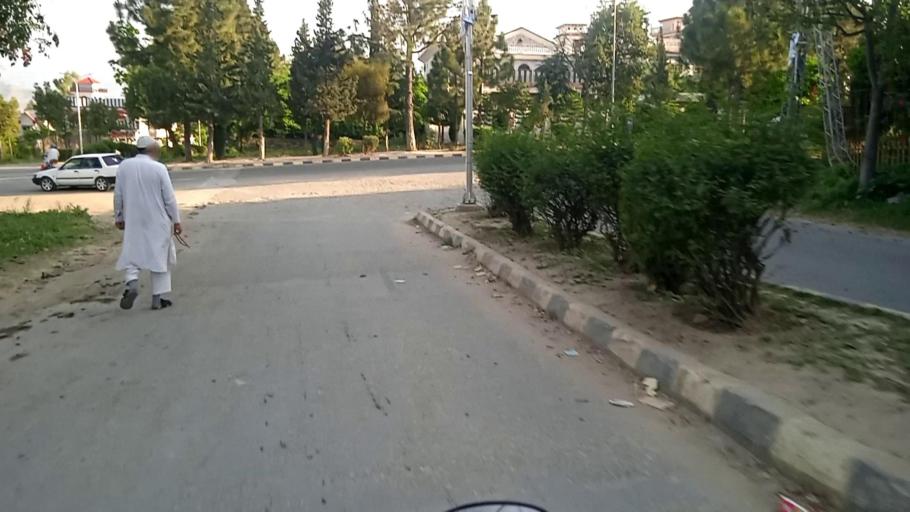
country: PK
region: Khyber Pakhtunkhwa
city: Mingora
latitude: 34.8301
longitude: 72.3426
